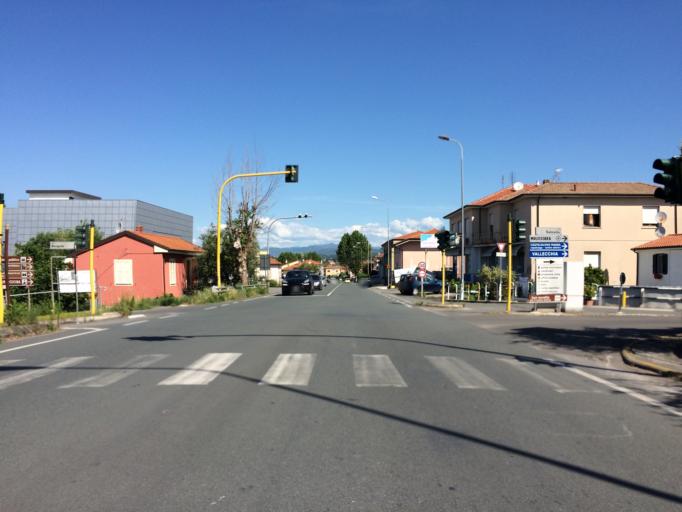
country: IT
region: Liguria
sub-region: Provincia di La Spezia
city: Colombiera-Molicciara
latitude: 44.0825
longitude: 10.0084
